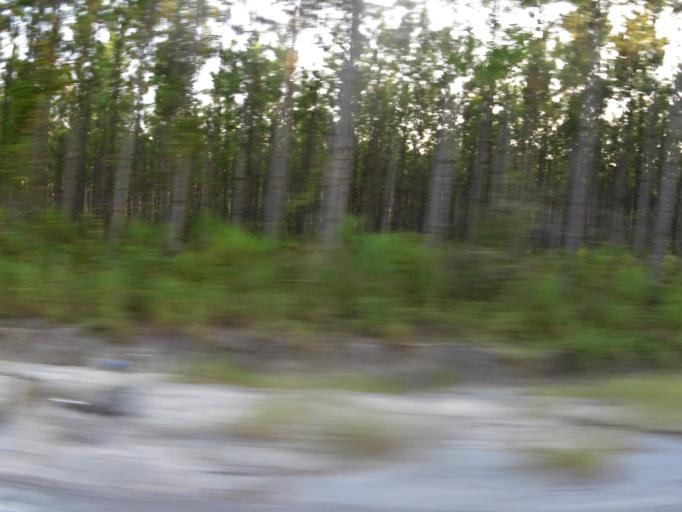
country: US
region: Florida
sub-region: Baker County
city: Macclenny
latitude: 30.3917
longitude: -82.0886
